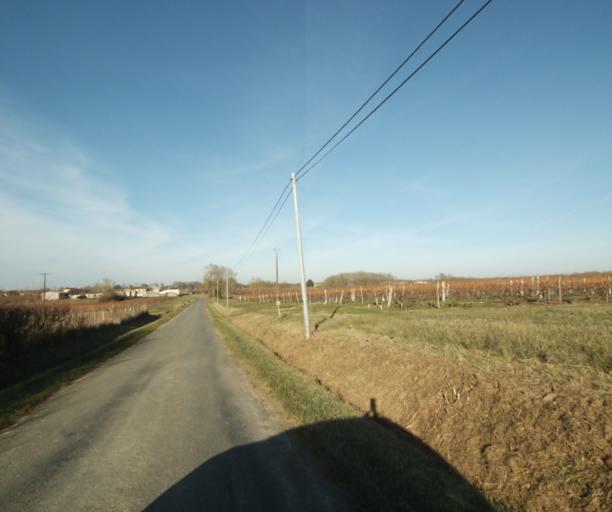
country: FR
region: Poitou-Charentes
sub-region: Departement de la Charente-Maritime
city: Burie
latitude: 45.7821
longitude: -0.4171
